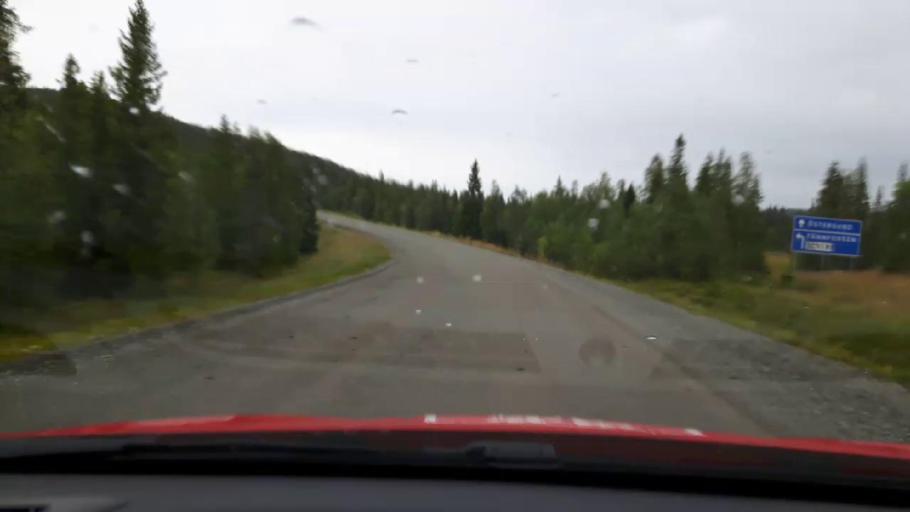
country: SE
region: Jaemtland
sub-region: Are Kommun
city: Are
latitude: 63.4330
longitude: 12.7287
